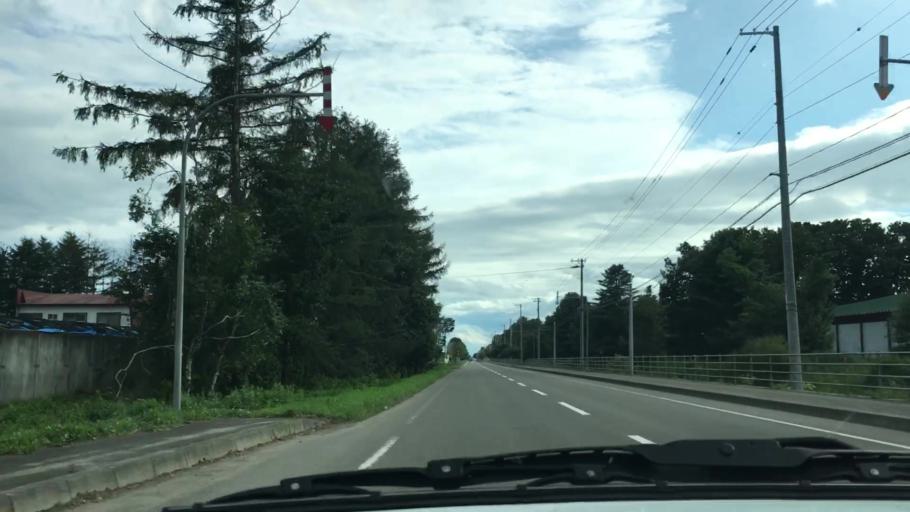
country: JP
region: Hokkaido
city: Otofuke
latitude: 43.2489
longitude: 143.2988
